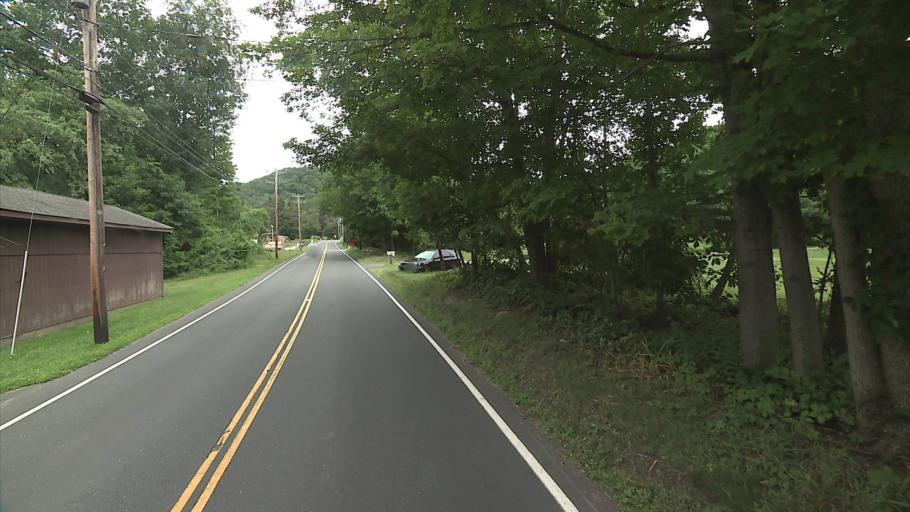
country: US
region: Connecticut
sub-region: Litchfield County
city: Winsted
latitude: 41.9860
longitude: -73.0457
